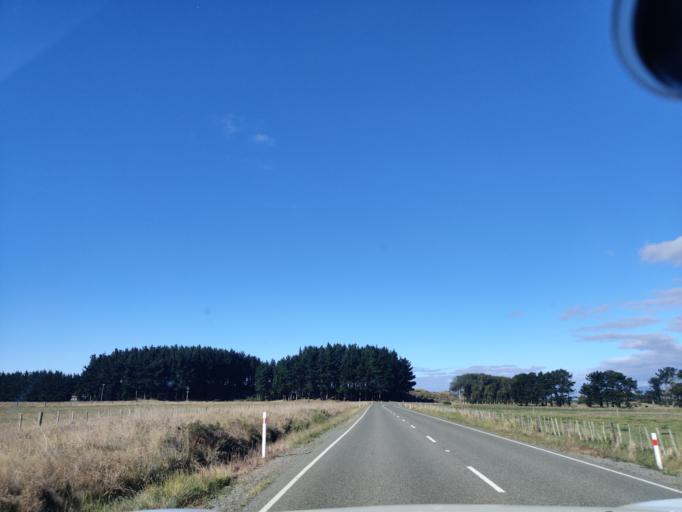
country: NZ
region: Manawatu-Wanganui
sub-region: Horowhenua District
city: Foxton
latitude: -40.4187
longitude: 175.4203
